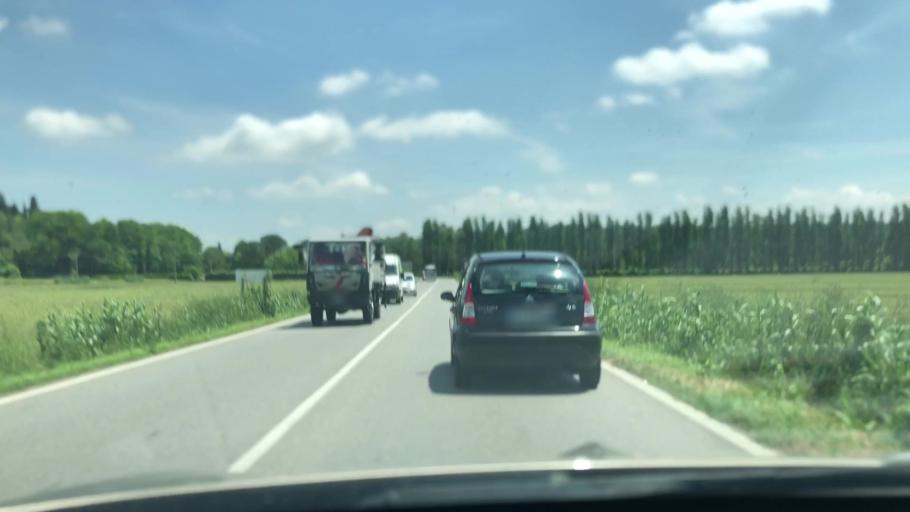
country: IT
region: Tuscany
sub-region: Province of Pisa
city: Treggiaia
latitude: 43.6171
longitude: 10.6764
